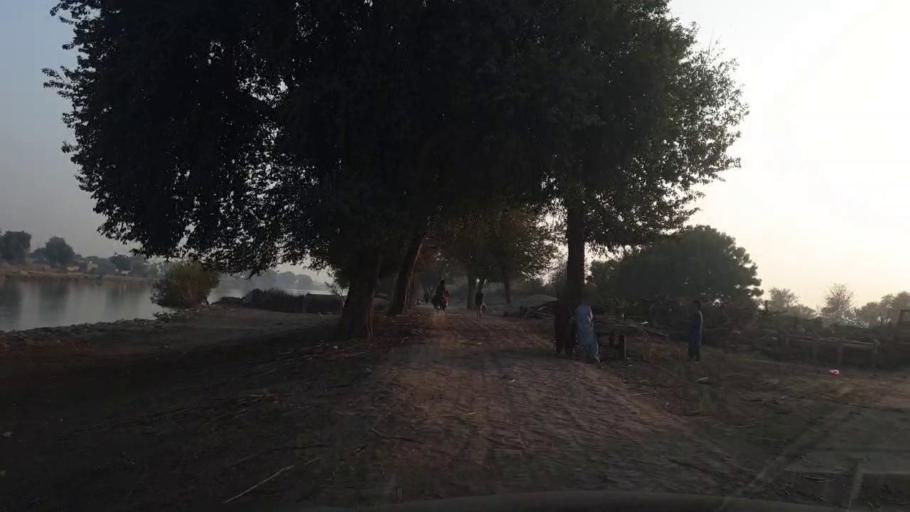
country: PK
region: Sindh
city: Ubauro
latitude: 28.3142
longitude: 69.7899
